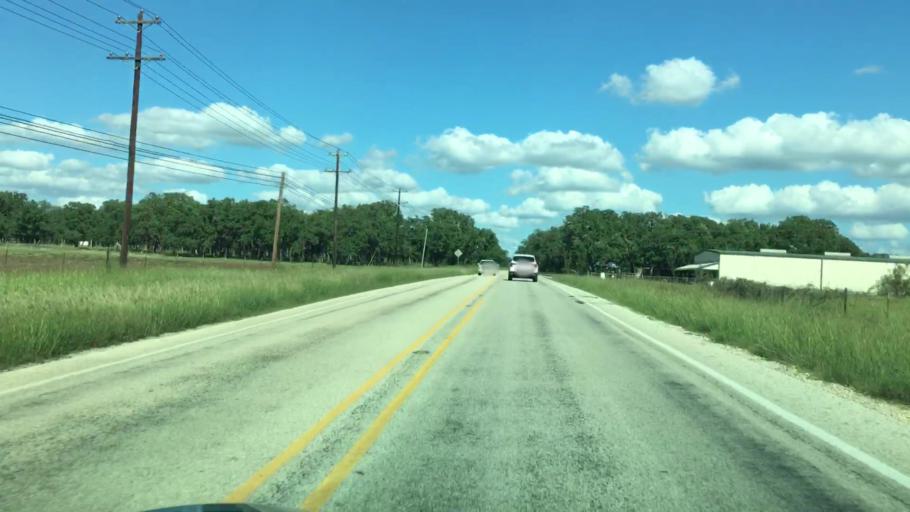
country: US
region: Texas
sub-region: Blanco County
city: Blanco
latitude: 30.0923
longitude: -98.3710
